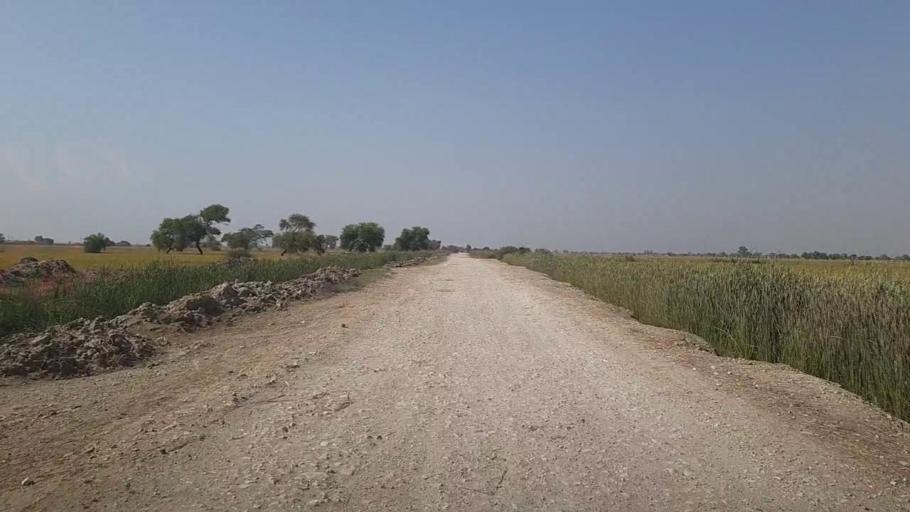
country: PK
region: Sindh
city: Kandhkot
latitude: 28.3969
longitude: 69.2708
